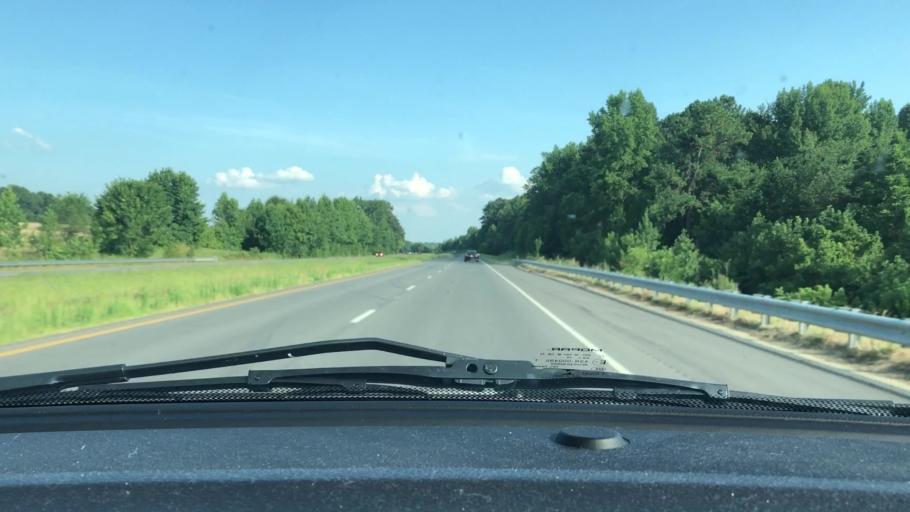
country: US
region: North Carolina
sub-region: Chatham County
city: Siler City
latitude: 35.6733
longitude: -79.4126
